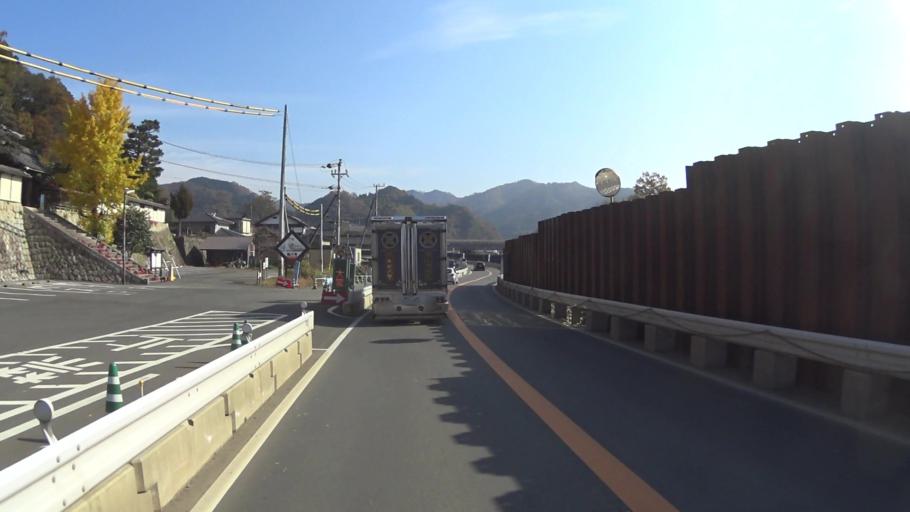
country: JP
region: Kyoto
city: Fukuchiyama
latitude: 35.3928
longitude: 135.1771
